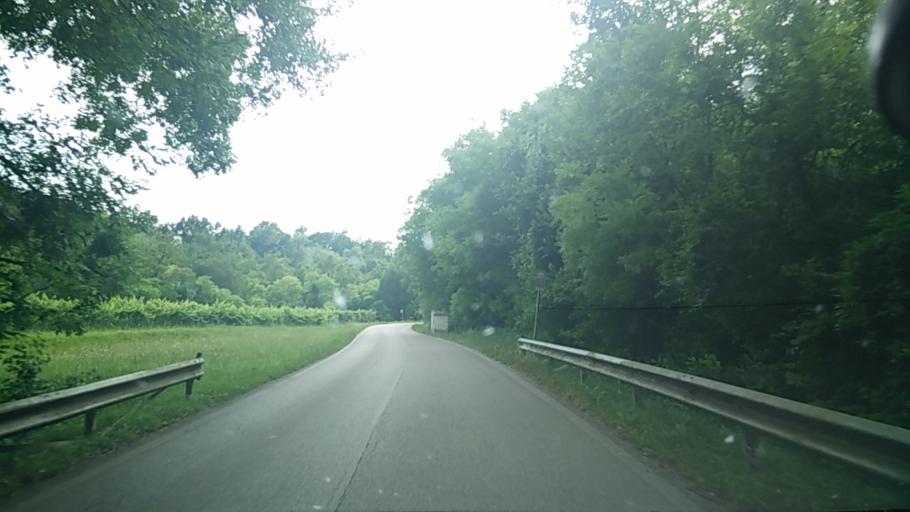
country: IT
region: Veneto
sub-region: Provincia di Treviso
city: Miane
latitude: 45.9236
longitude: 12.0953
